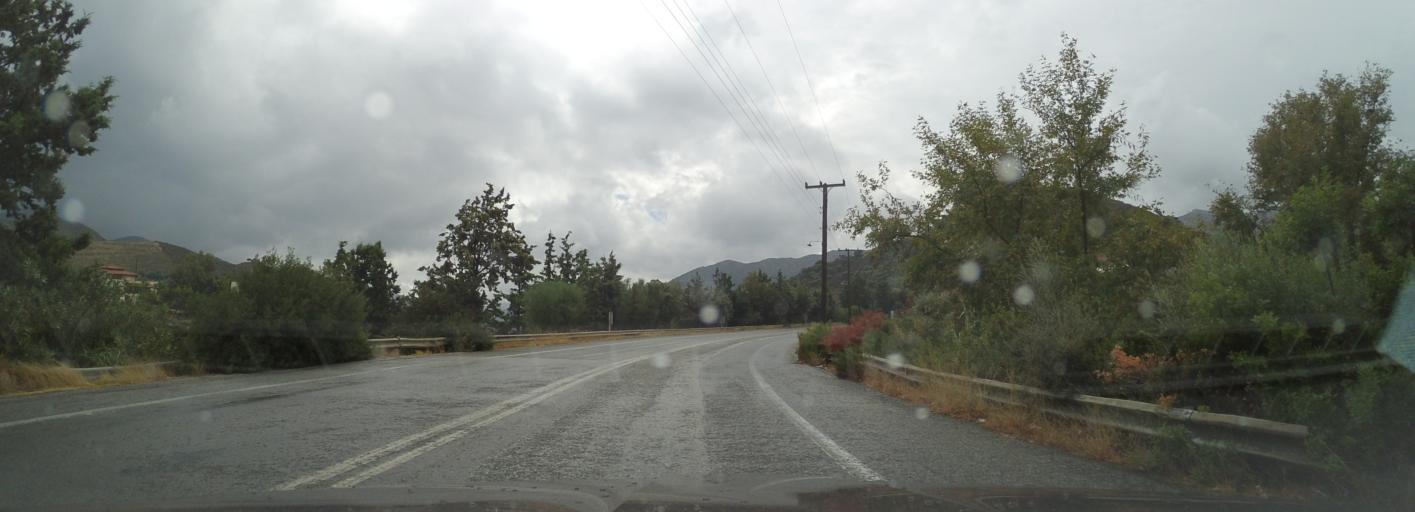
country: GR
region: Crete
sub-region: Nomos Irakleiou
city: Tilisos
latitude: 35.3941
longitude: 24.9492
